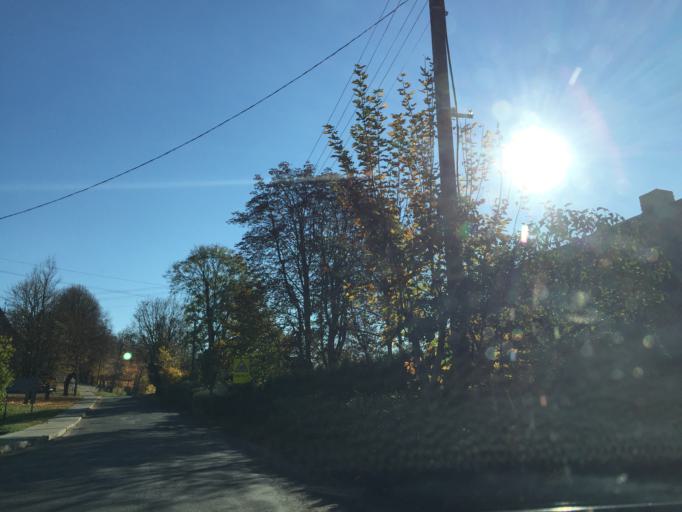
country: LT
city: Plateliai
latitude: 56.0420
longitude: 21.8153
